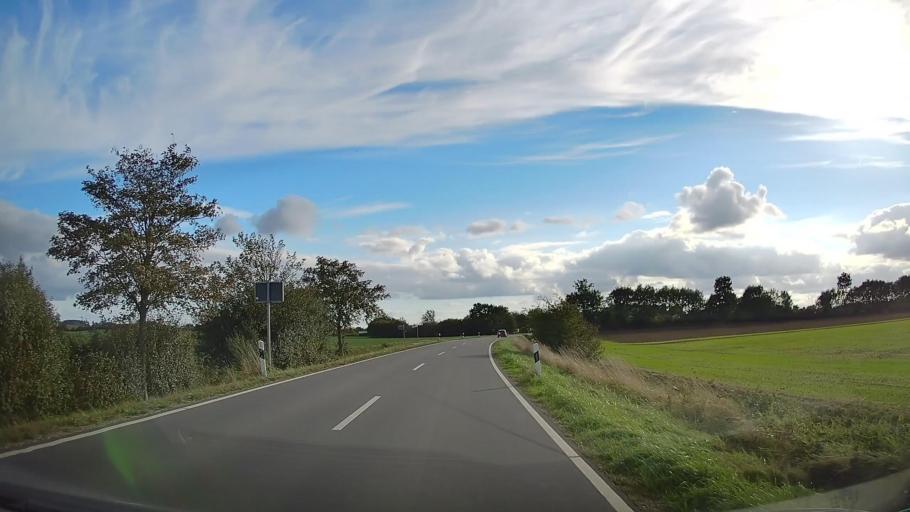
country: DE
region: Schleswig-Holstein
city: Pommerby
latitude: 54.7643
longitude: 9.9468
